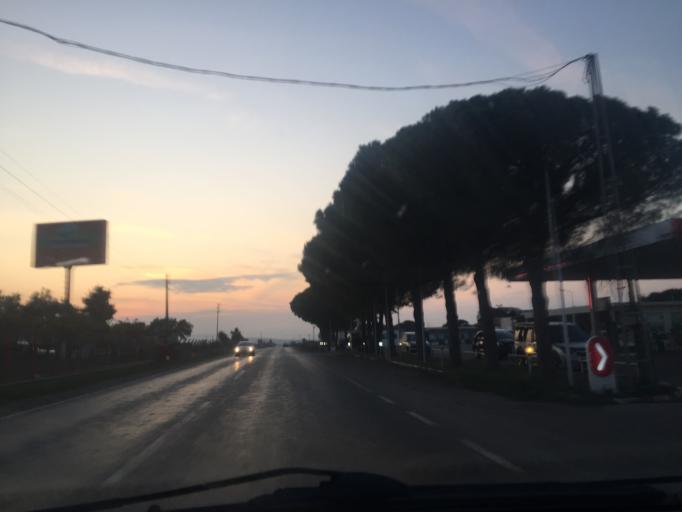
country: TR
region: Canakkale
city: Bayramic
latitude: 39.7766
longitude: 26.4860
